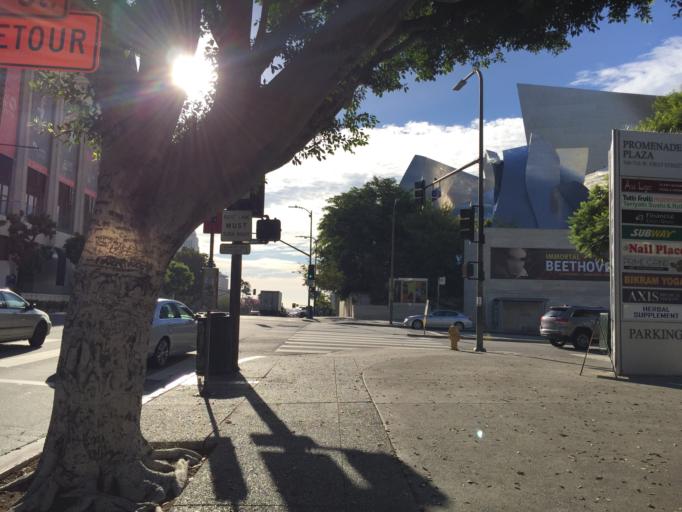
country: US
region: California
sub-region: Los Angeles County
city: Los Angeles
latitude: 34.0565
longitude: -118.2502
